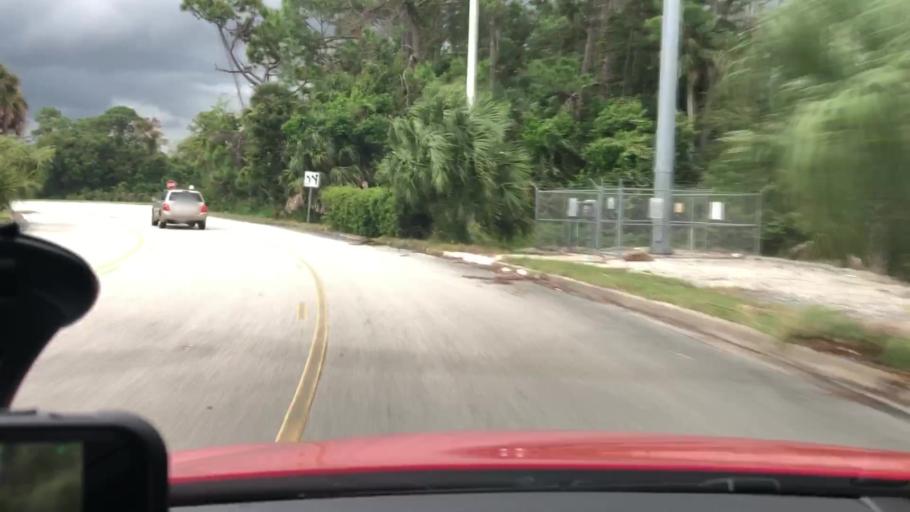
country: US
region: Florida
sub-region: Volusia County
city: Daytona Beach
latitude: 29.1985
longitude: -81.0669
